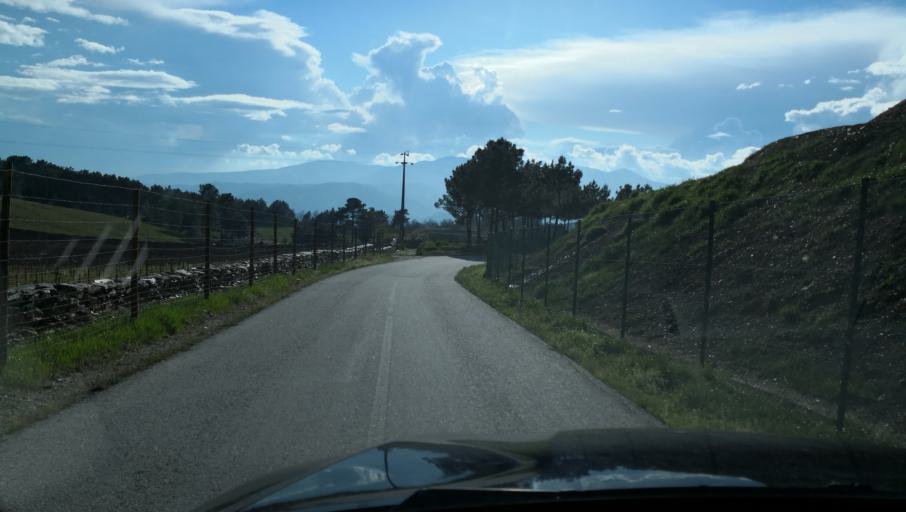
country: PT
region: Vila Real
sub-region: Vila Real
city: Vila Real
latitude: 41.2518
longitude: -7.7110
